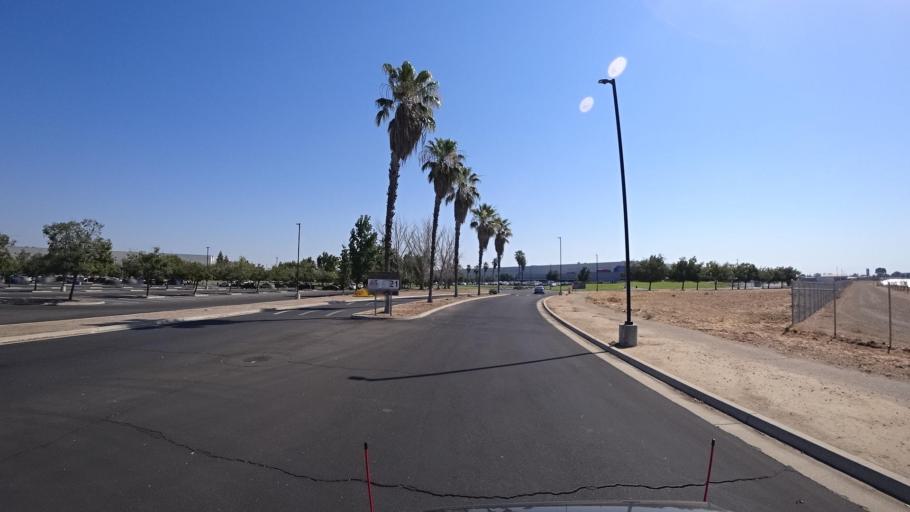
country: US
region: California
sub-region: Fresno County
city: Tarpey Village
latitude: 36.7821
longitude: -119.7088
